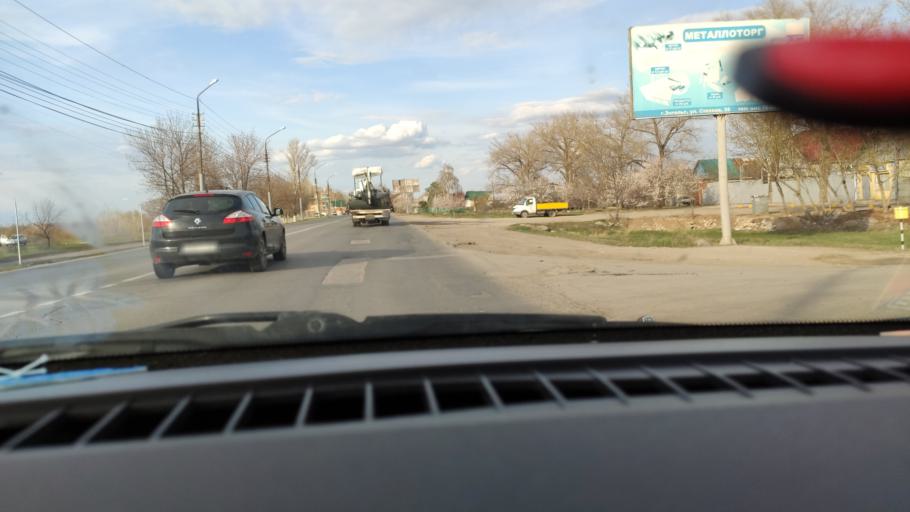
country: RU
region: Saratov
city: Engel's
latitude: 51.4512
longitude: 46.0827
